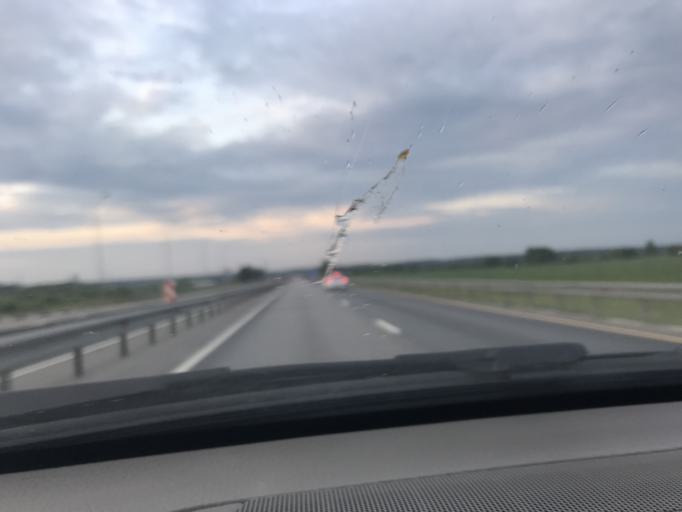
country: RU
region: Kaluga
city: Obninsk
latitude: 55.0376
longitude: 36.5892
